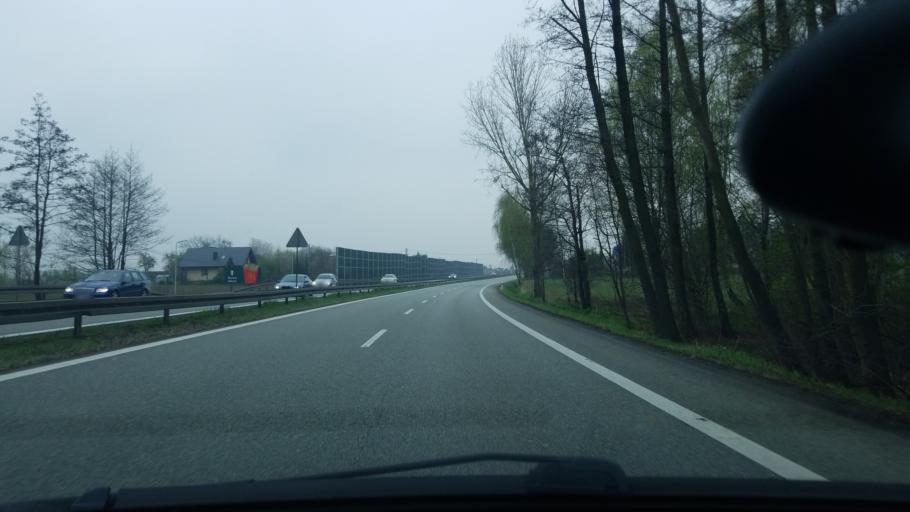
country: PL
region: Silesian Voivodeship
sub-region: Powiat pszczynski
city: Pawlowice
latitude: 49.9800
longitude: 18.7159
